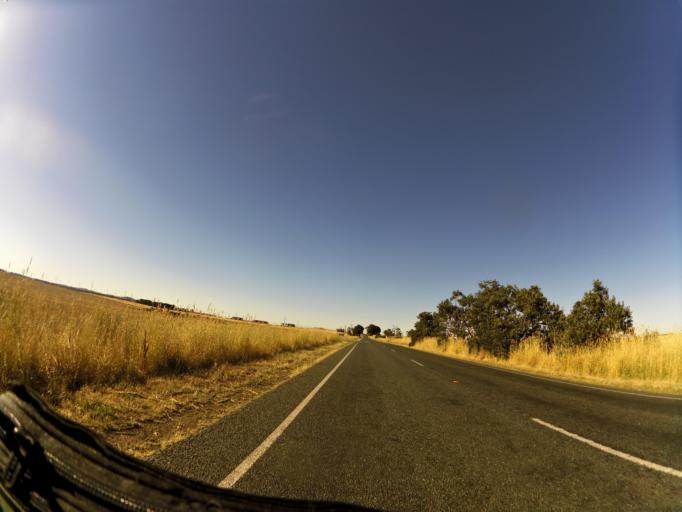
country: AU
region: Victoria
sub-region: Ballarat North
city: Delacombe
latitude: -37.5740
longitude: 143.3567
